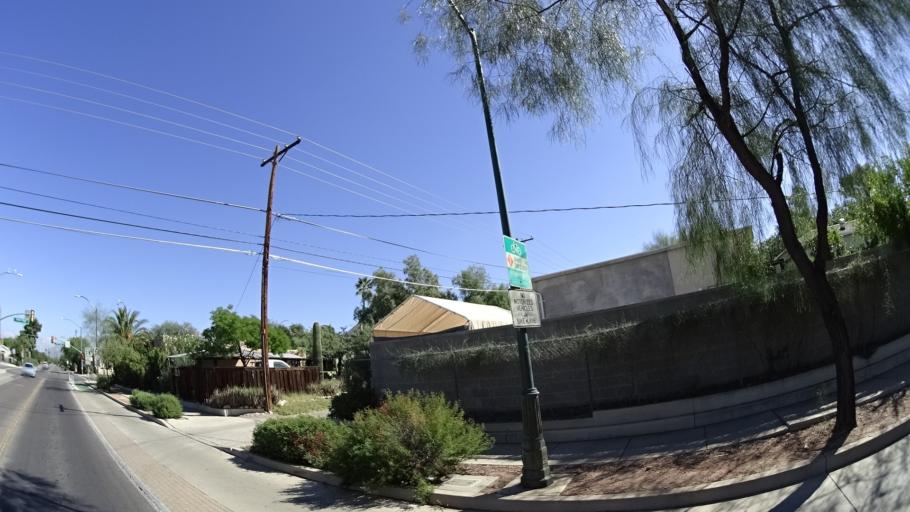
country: US
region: Arizona
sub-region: Pima County
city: Tucson
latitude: 32.2492
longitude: -110.9525
